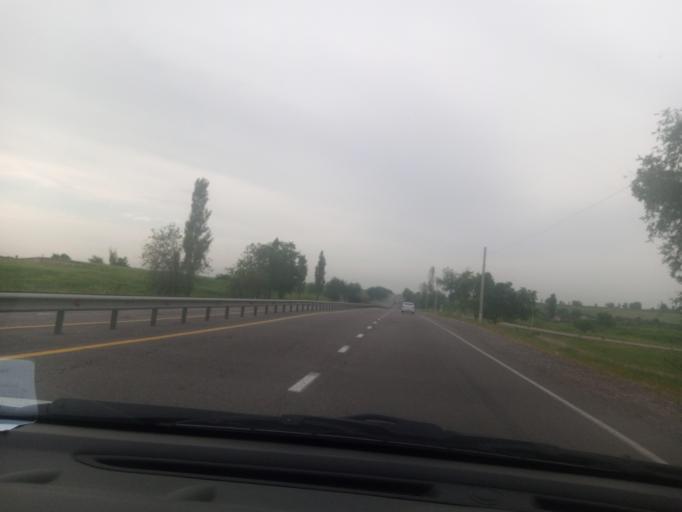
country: UZ
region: Toshkent
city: Tuytepa
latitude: 41.0621
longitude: 69.4834
